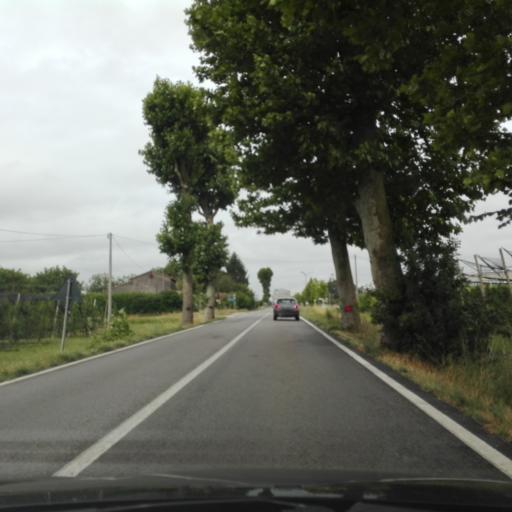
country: IT
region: Veneto
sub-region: Provincia di Rovigo
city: Costa di Rovigo
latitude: 45.0763
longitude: 11.6826
